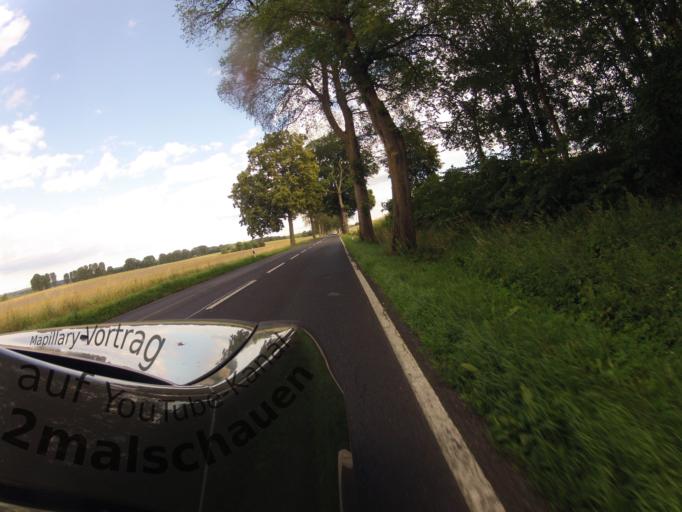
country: DE
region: Mecklenburg-Vorpommern
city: Seebad Bansin
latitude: 53.8869
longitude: 14.1060
